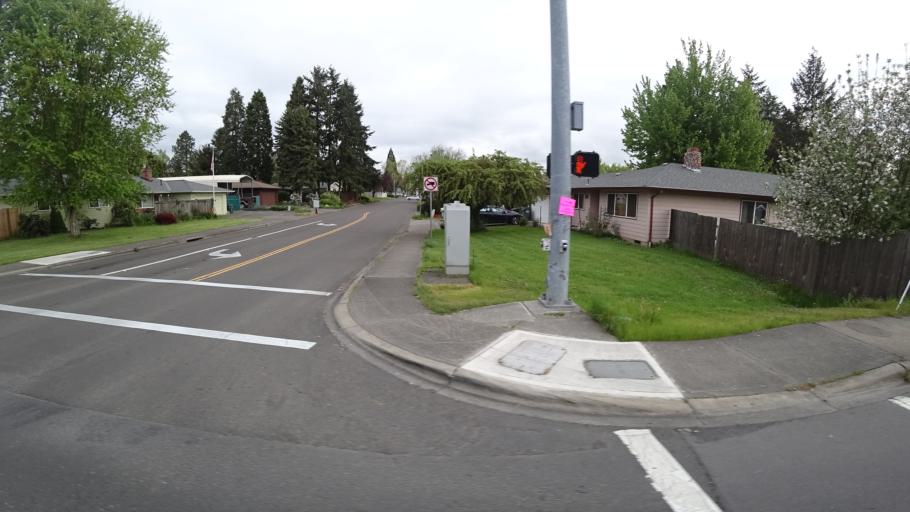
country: US
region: Oregon
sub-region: Washington County
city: Hillsboro
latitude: 45.5200
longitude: -122.9497
